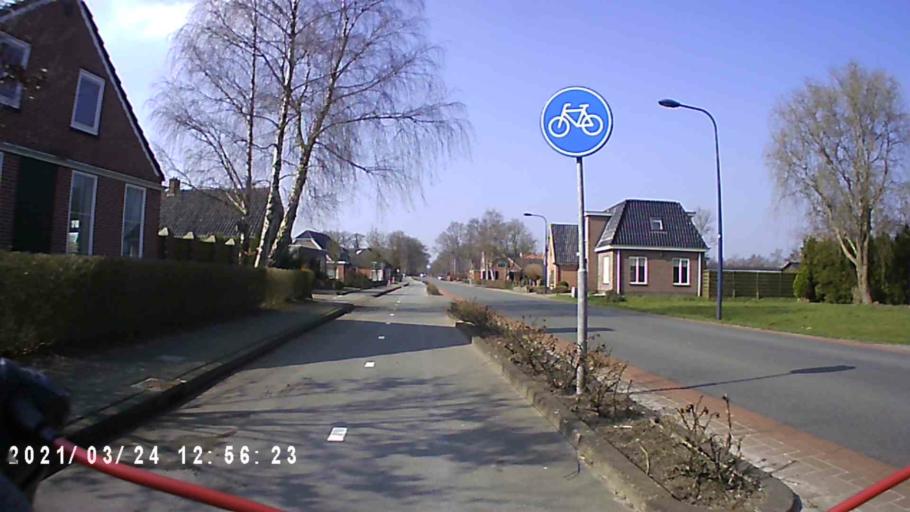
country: NL
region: Groningen
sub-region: Gemeente Grootegast
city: Grootegast
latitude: 53.1523
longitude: 6.3066
